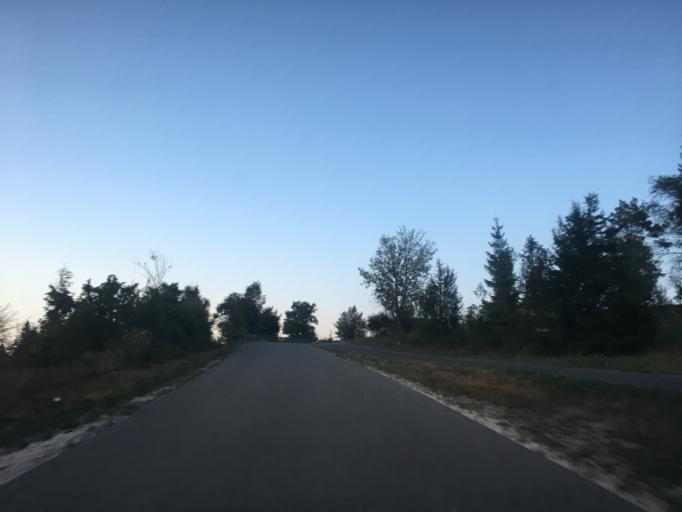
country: DE
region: Baden-Wuerttemberg
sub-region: Tuebingen Region
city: Hayingen
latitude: 48.2812
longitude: 9.4520
